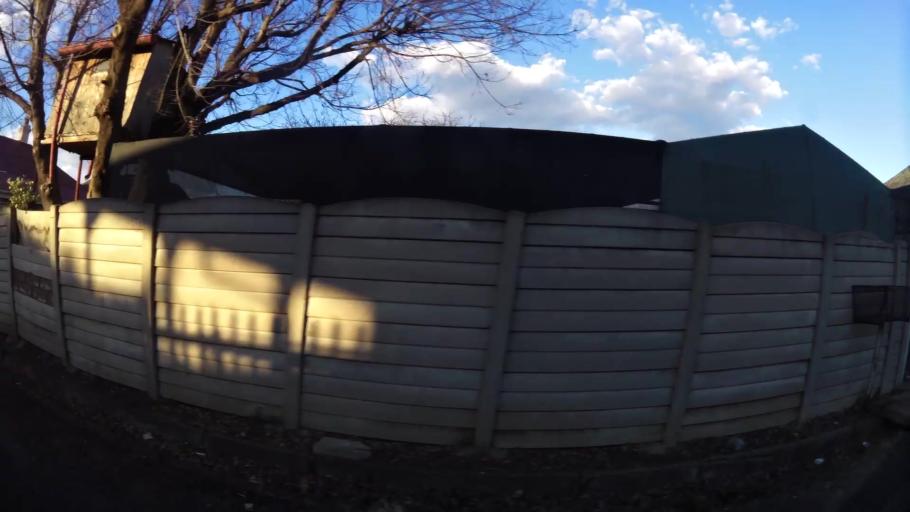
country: ZA
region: North-West
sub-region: Dr Kenneth Kaunda District Municipality
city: Potchefstroom
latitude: -26.7174
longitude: 27.0917
